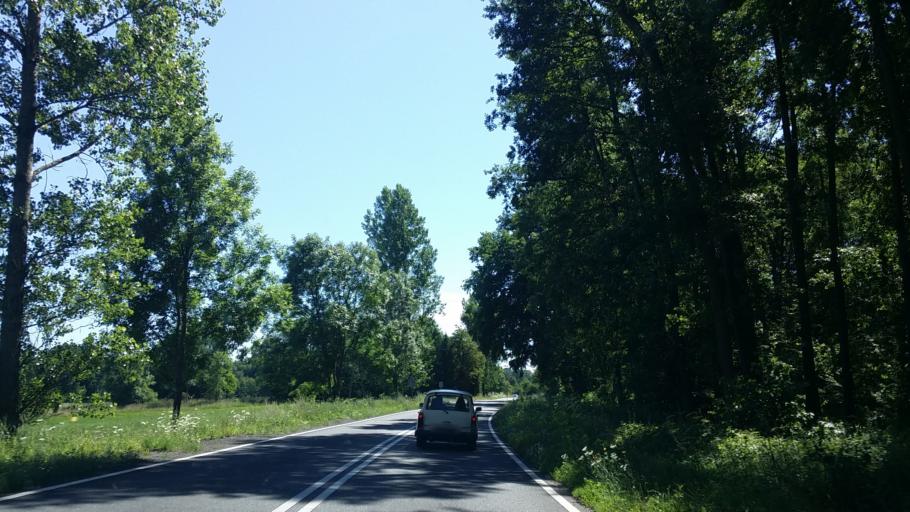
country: PL
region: West Pomeranian Voivodeship
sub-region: Powiat stargardzki
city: Insko
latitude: 53.4743
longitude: 15.5781
